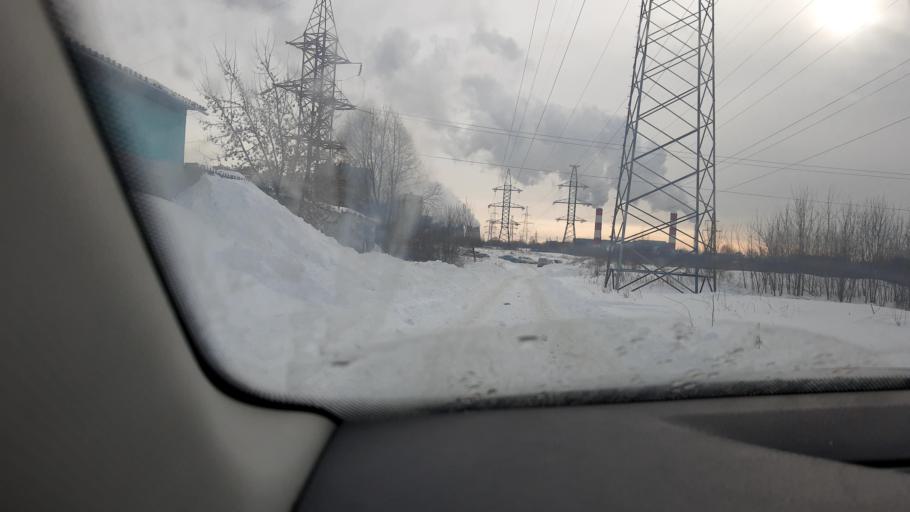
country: RU
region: Moskovskaya
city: Biryulevo Zapadnoye
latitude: 55.5975
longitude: 37.6395
